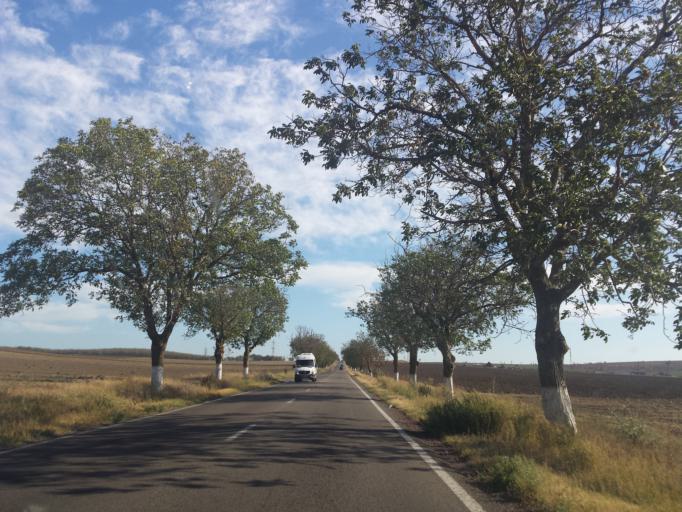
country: RO
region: Tulcea
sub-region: Comuna Frecatei
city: Cataloi
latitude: 45.1208
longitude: 28.7508
